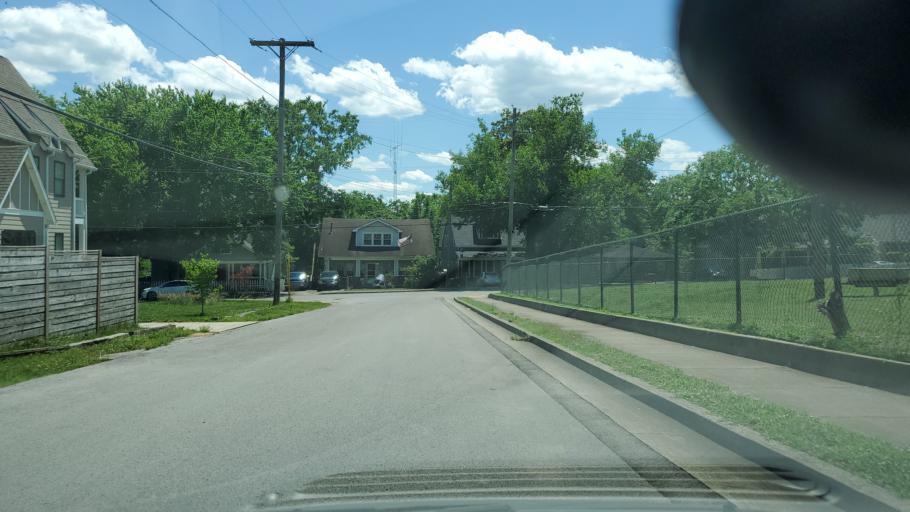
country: US
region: Tennessee
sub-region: Davidson County
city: Nashville
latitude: 36.1911
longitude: -86.7471
